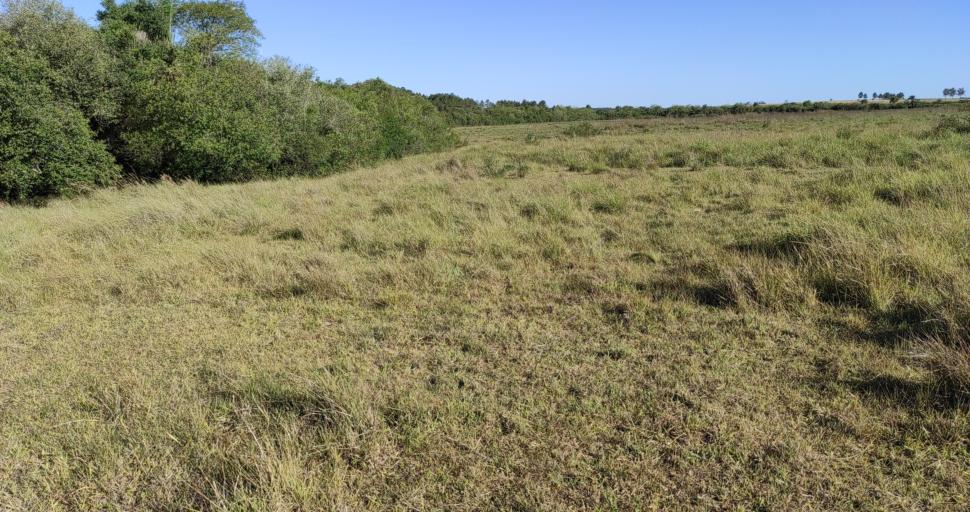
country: PY
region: Itapua
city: San Juan del Parana
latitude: -27.4515
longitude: -56.0550
